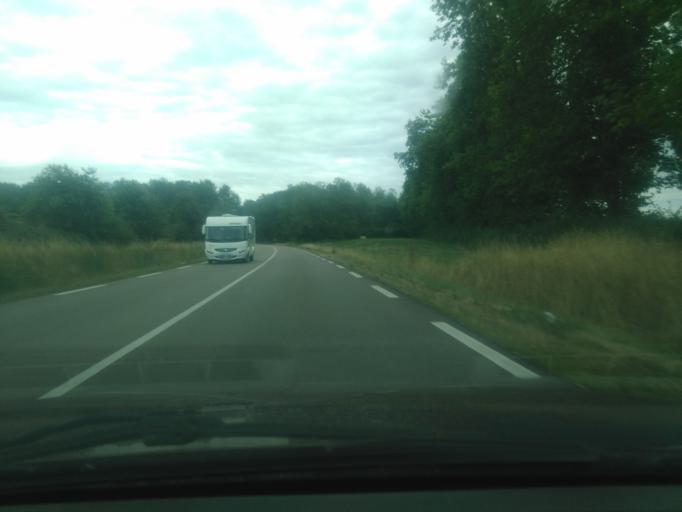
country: FR
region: Bourgogne
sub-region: Departement de la Nievre
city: Saint-Pierre-le-Moutier
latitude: 46.8019
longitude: 3.0955
